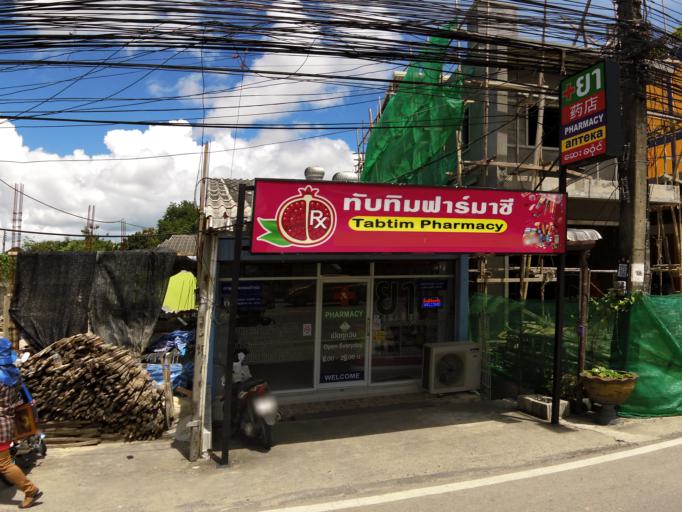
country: TH
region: Phuket
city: Ban Chalong
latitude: 7.8432
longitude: 98.3346
